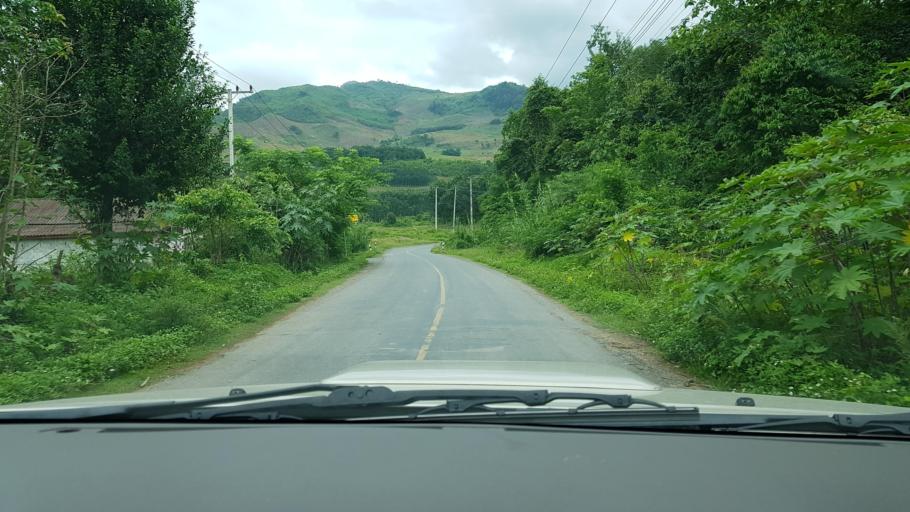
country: LA
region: Loungnamtha
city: Muang Nale
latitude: 20.1862
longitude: 101.5187
